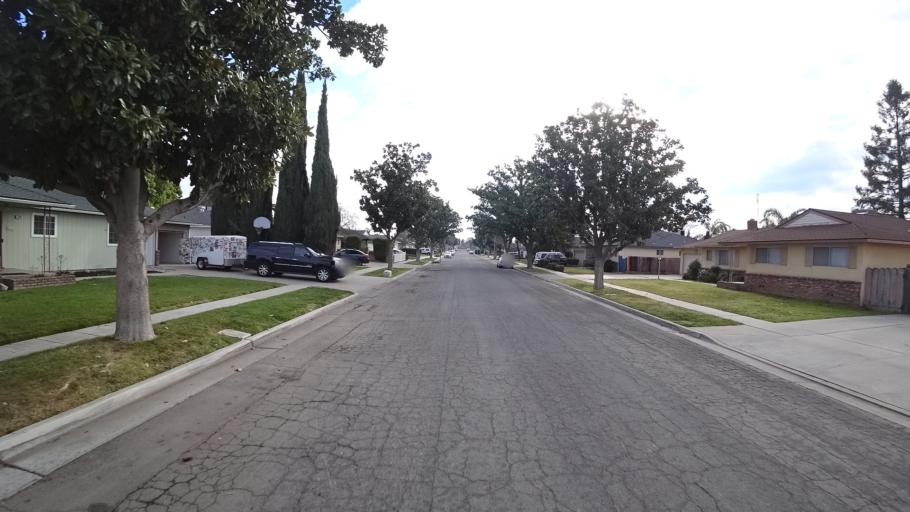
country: US
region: California
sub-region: Fresno County
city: Clovis
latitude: 36.8289
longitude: -119.7663
